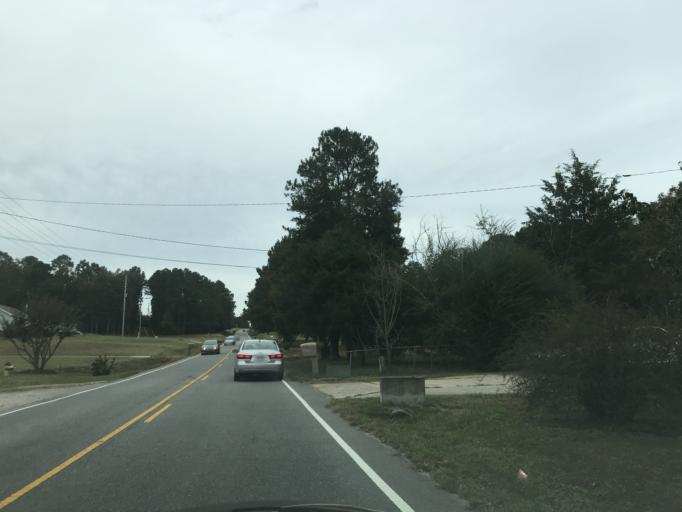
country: US
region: North Carolina
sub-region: Wake County
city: Rolesville
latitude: 35.9164
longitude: -78.5061
